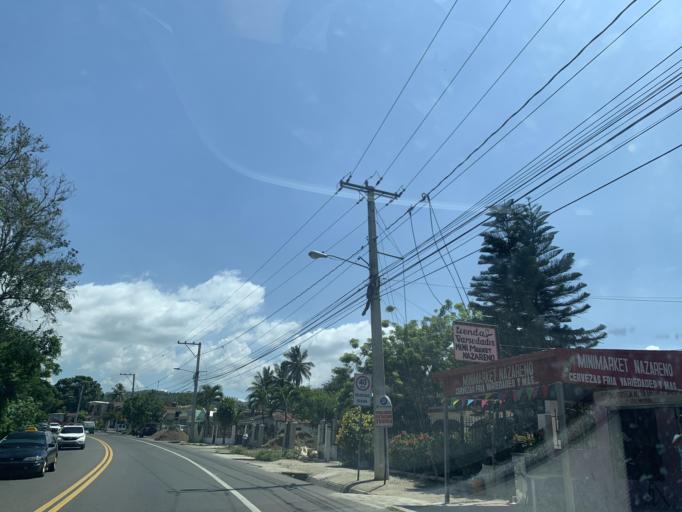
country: DO
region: Puerto Plata
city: Imbert
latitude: 19.7233
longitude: -70.8325
